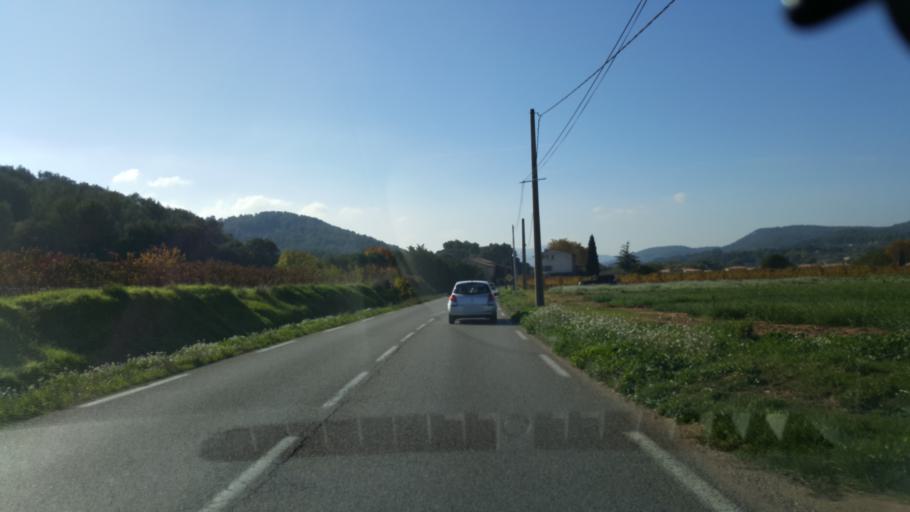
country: FR
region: Provence-Alpes-Cote d'Azur
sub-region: Departement du Var
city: Saint-Zacharie
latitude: 43.3779
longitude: 5.6870
